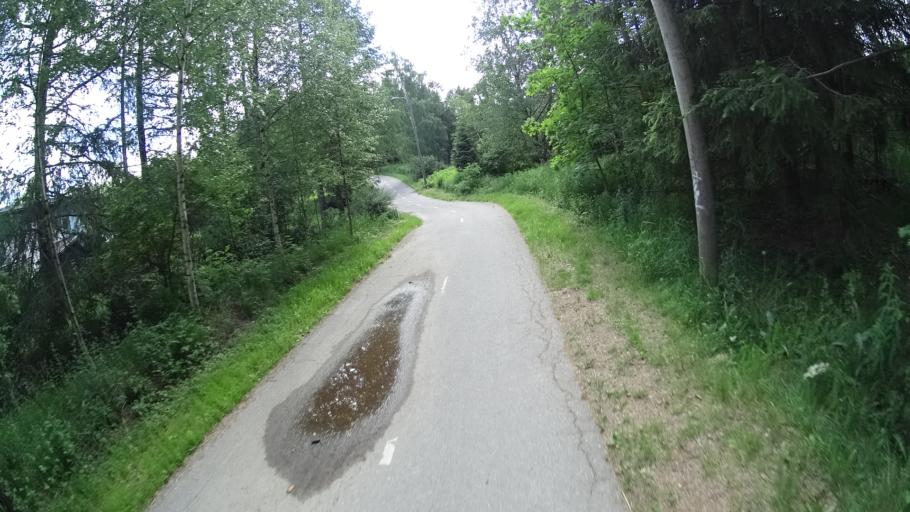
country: FI
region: Uusimaa
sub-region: Helsinki
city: Vantaa
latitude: 60.2421
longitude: 25.0095
